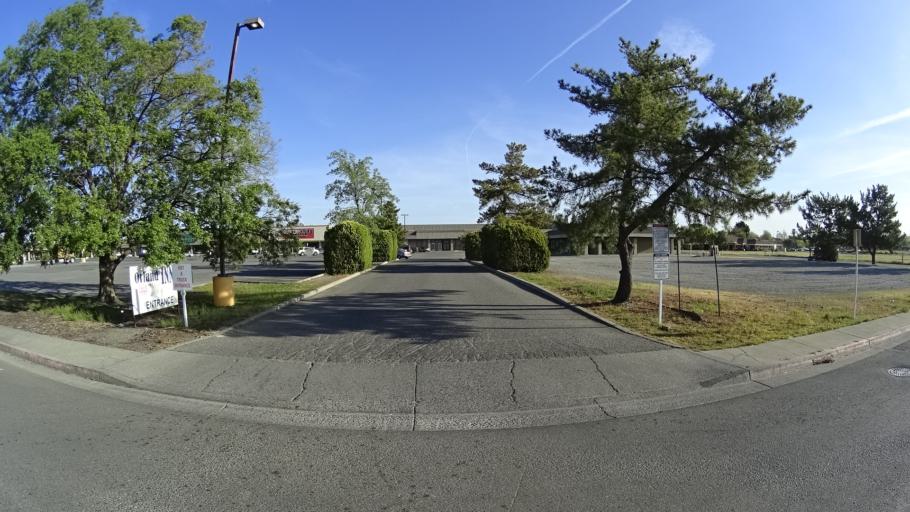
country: US
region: California
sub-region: Glenn County
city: Orland
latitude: 39.7404
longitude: -122.2032
